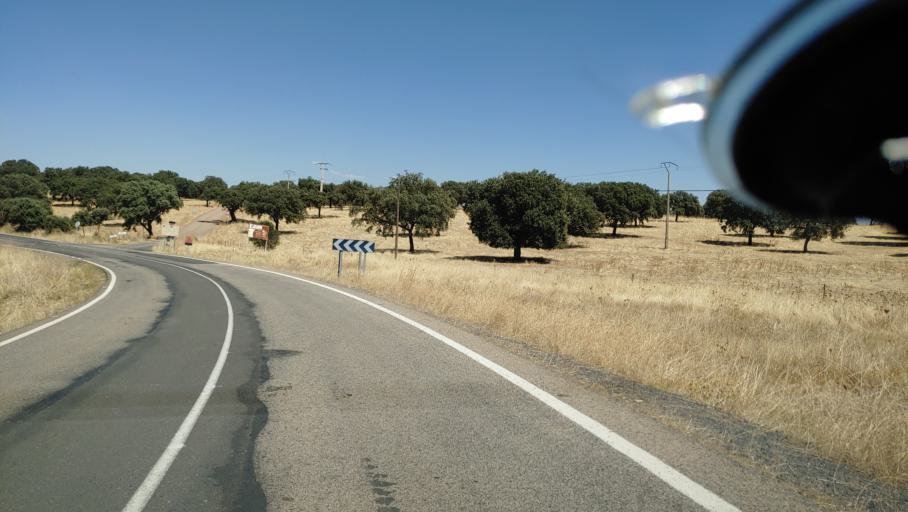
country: ES
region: Castille-La Mancha
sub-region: Provincia de Ciudad Real
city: Alamillo
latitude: 38.7401
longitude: -4.7017
